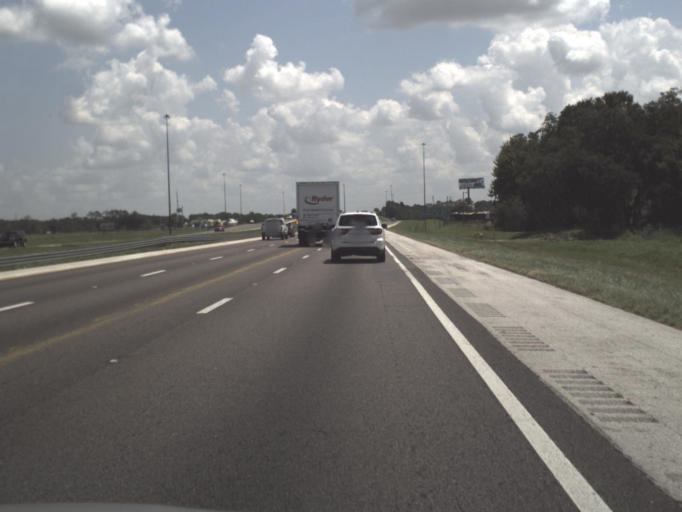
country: US
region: Florida
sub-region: Hillsborough County
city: Dover
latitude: 28.0212
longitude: -82.2526
